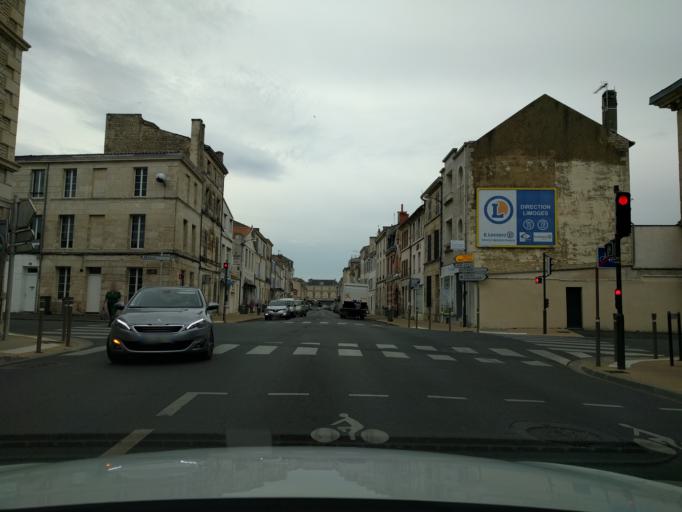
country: FR
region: Poitou-Charentes
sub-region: Departement des Deux-Sevres
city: Niort
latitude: 46.3205
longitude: -0.4587
